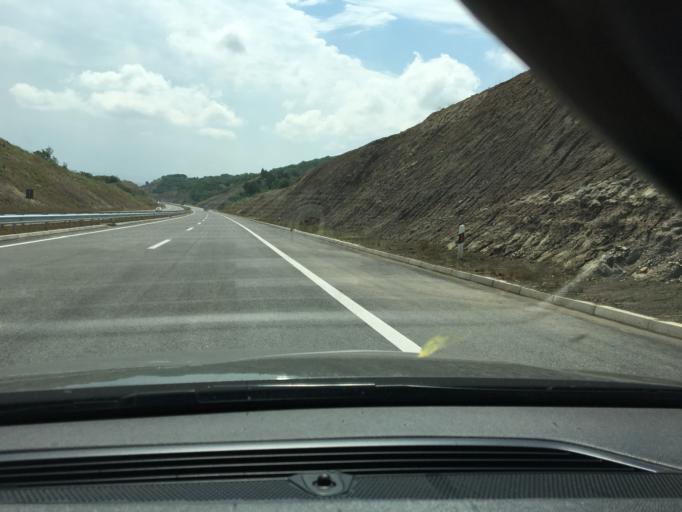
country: MK
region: Sveti Nikole
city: Gorobinci
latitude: 41.9249
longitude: 21.8386
